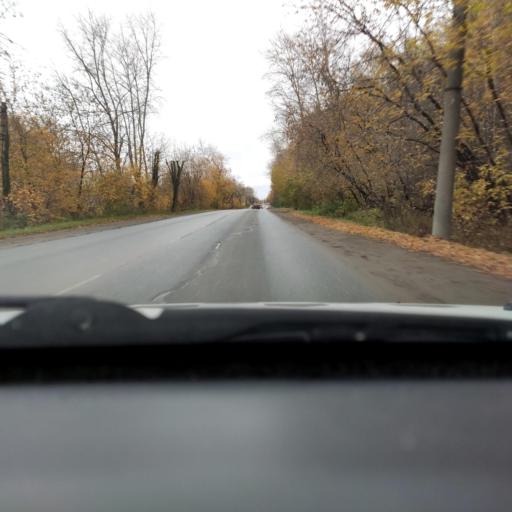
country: RU
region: Perm
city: Perm
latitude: 58.0803
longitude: 56.3502
